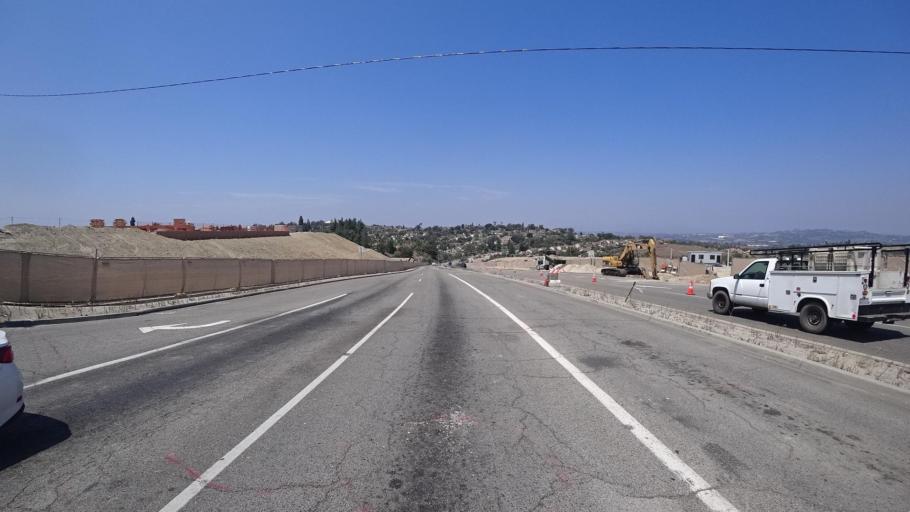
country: US
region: California
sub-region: San Diego County
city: Vista
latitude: 33.2210
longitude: -117.2595
